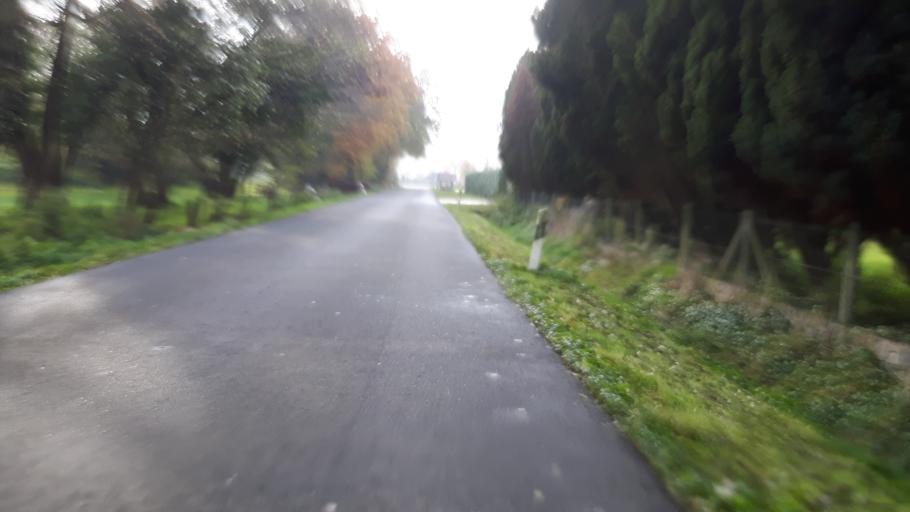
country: DE
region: Lower Saxony
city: Ganderkesee
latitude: 53.0169
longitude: 8.5860
